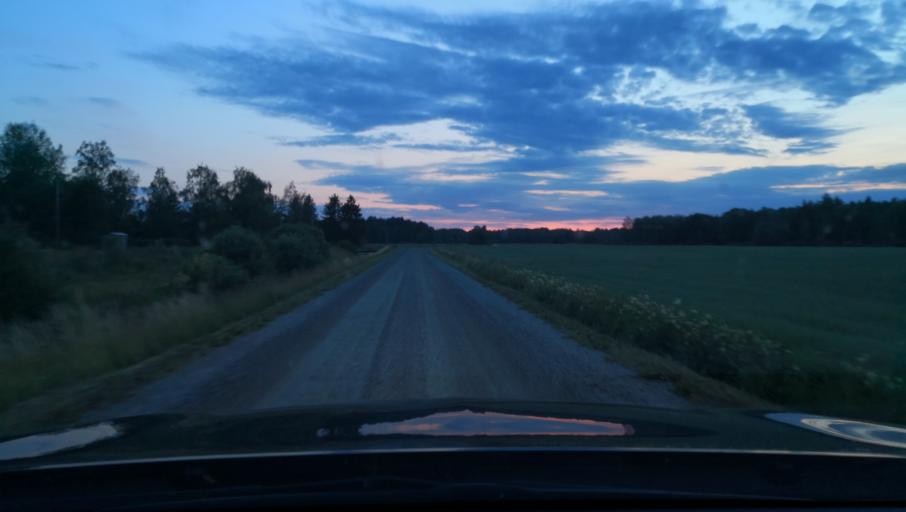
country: SE
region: Uppsala
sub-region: Heby Kommun
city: OEstervala
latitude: 60.0124
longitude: 17.3141
